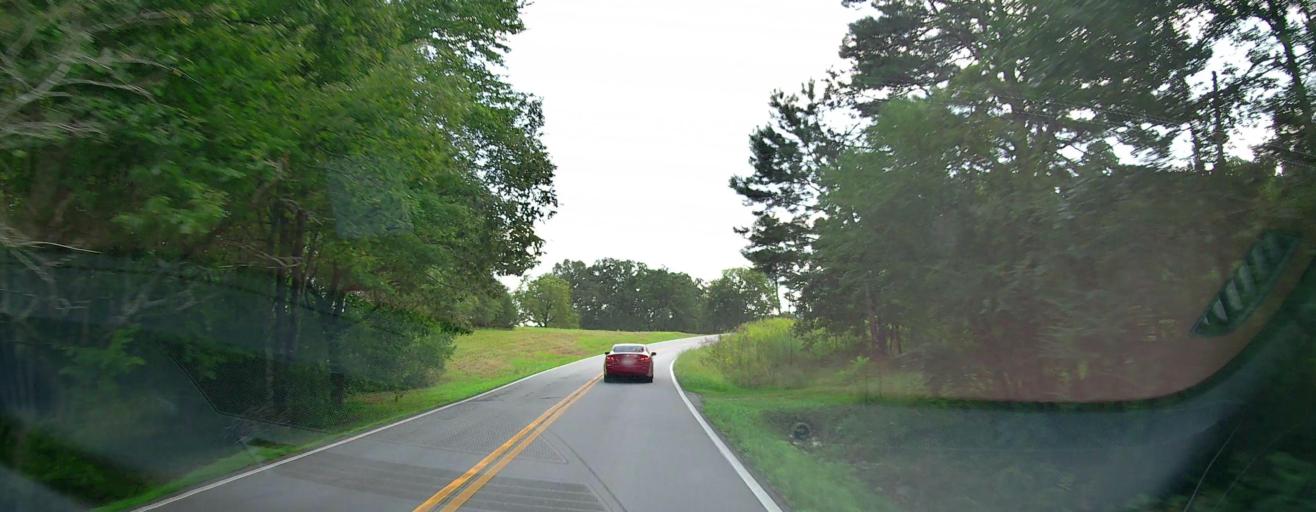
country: US
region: Georgia
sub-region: Catoosa County
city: Ringgold
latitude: 34.9231
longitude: -85.0848
